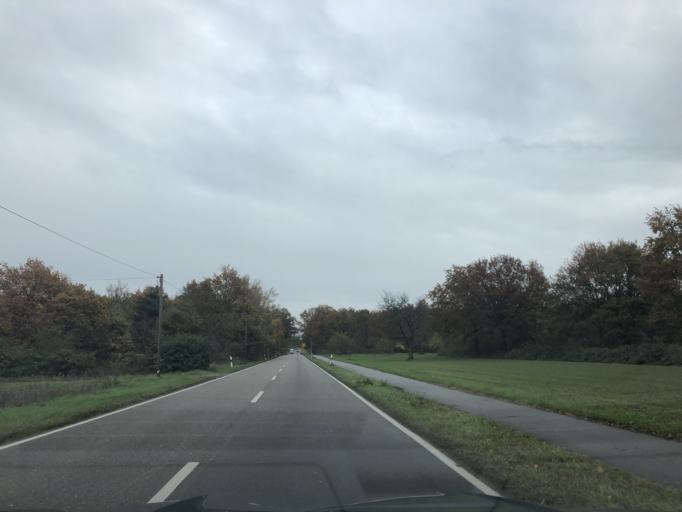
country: DE
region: Rheinland-Pfalz
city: Bellheim
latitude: 49.1882
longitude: 8.3008
